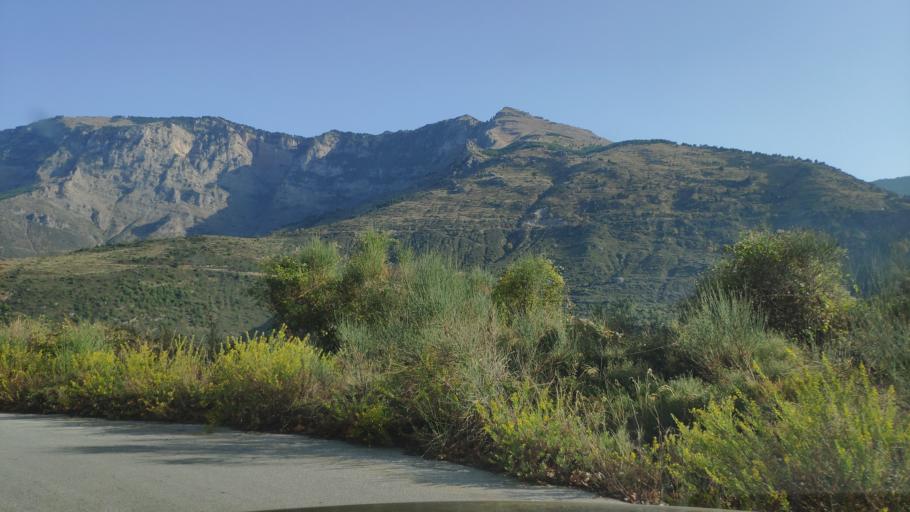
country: GR
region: West Greece
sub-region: Nomos Achaias
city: Aiyira
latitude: 38.0682
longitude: 22.3827
